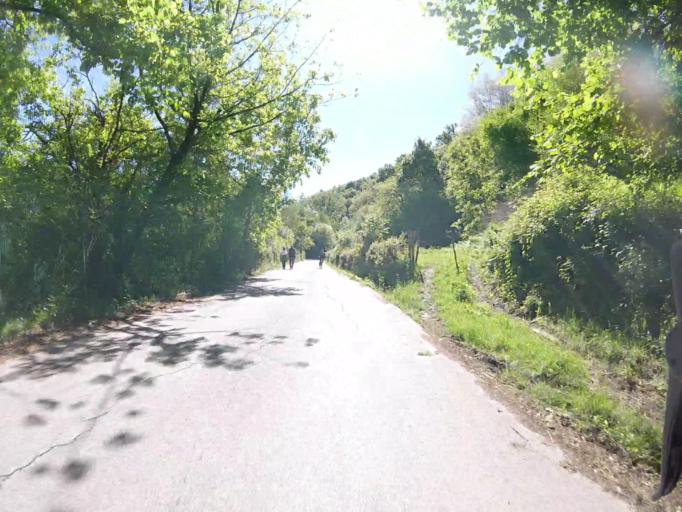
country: ES
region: Navarre
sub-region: Provincia de Navarra
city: Bera
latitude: 43.2746
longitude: -1.7109
